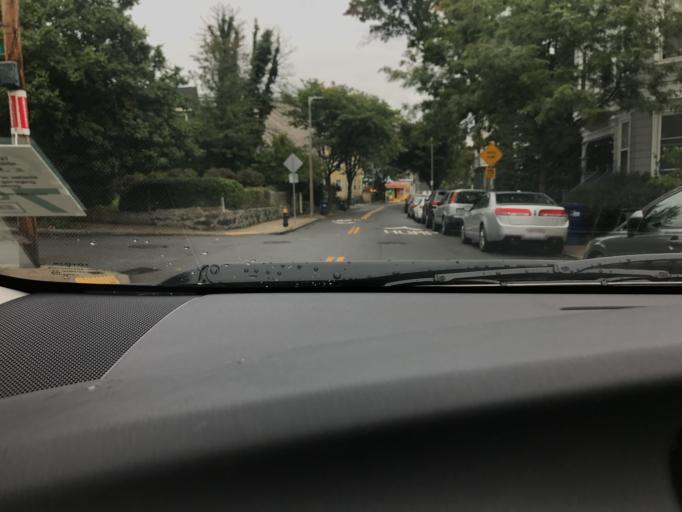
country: US
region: Massachusetts
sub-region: Norfolk County
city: Brookline
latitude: 42.3237
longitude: -71.1093
